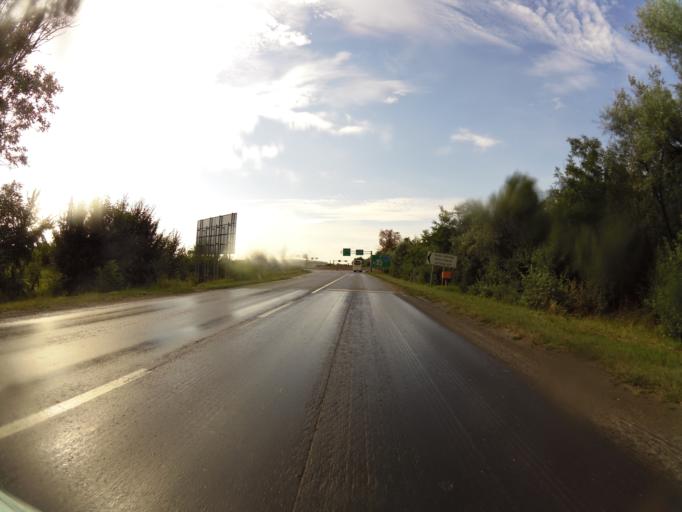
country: HU
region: Csongrad
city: Szeged
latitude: 46.2810
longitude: 20.0940
